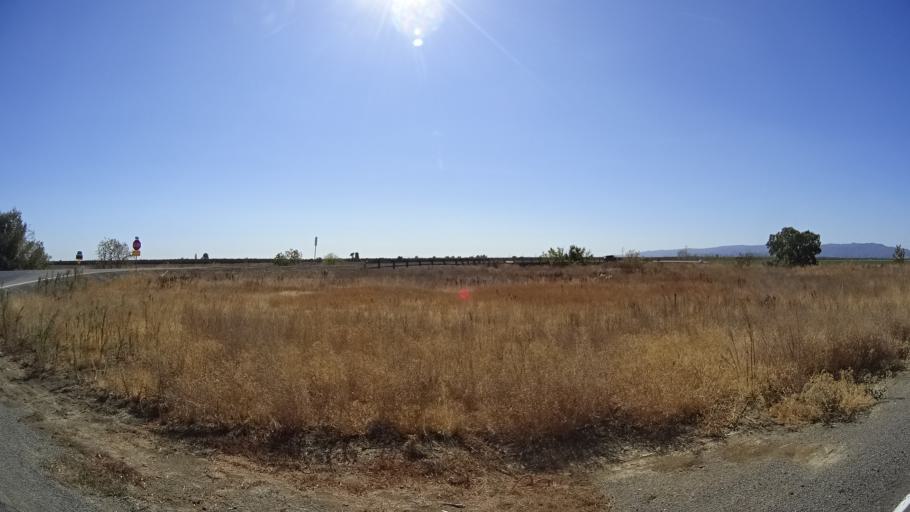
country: US
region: California
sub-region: Yolo County
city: Winters
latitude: 38.5616
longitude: -121.8985
